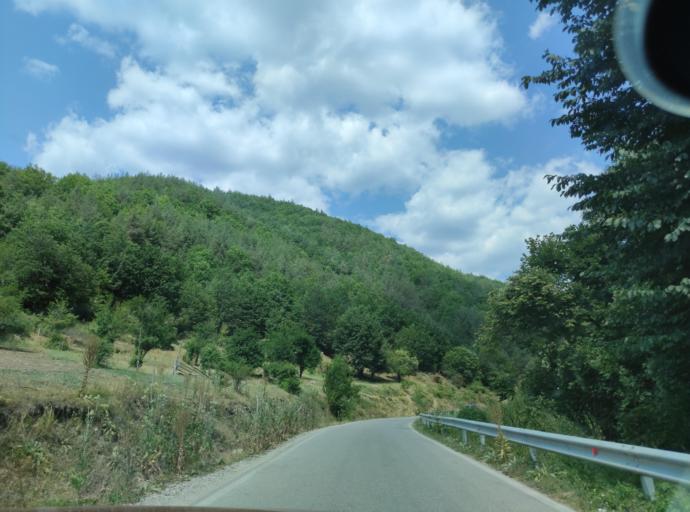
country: BG
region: Blagoevgrad
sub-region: Obshtina Belitsa
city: Belitsa
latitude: 42.0031
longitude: 23.5512
